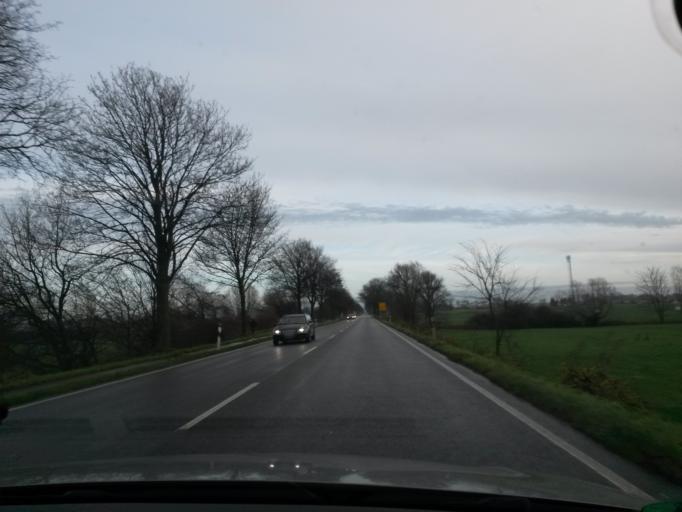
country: DE
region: North Rhine-Westphalia
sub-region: Regierungsbezirk Dusseldorf
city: Alpen
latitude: 51.6015
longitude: 6.5459
